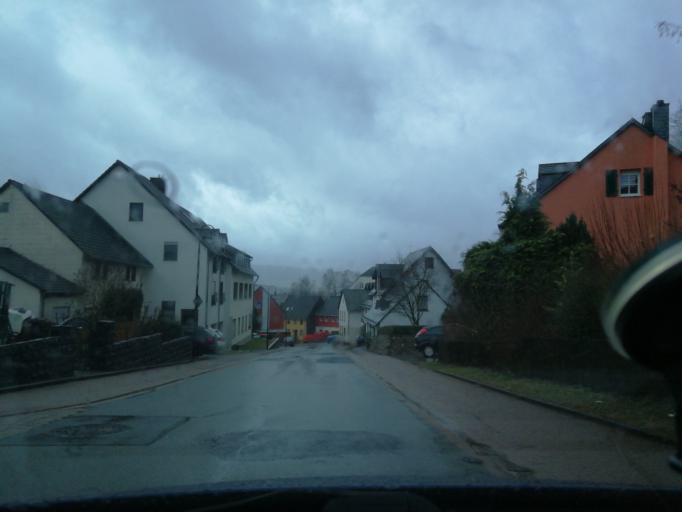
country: DE
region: Rheinland-Pfalz
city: Thalfang
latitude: 49.7560
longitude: 6.9950
